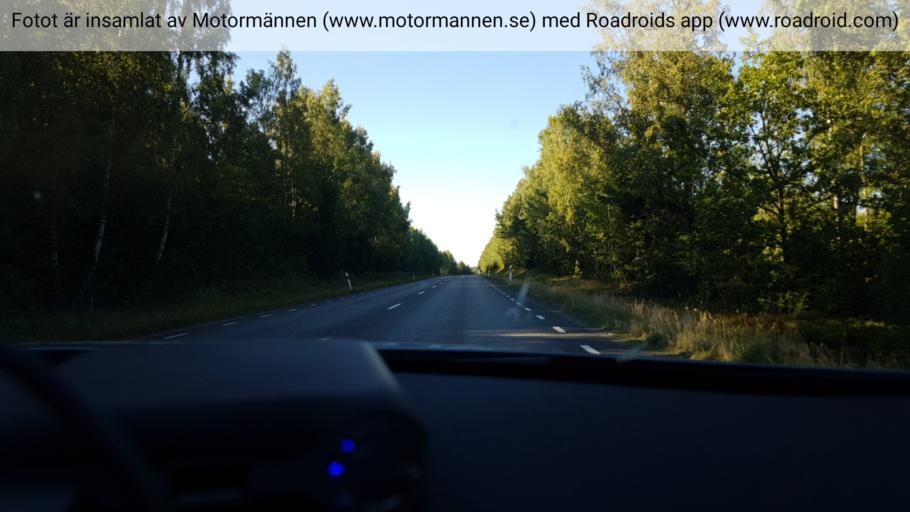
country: SE
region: Joenkoeping
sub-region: Habo Kommun
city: Habo
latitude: 57.9717
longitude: 14.1052
